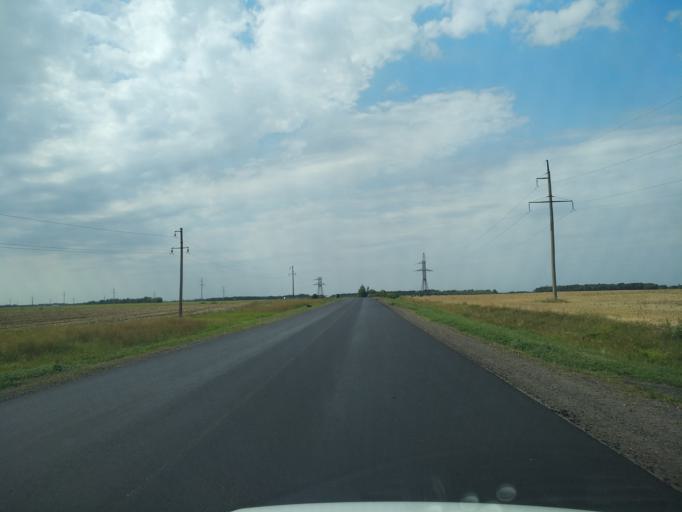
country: RU
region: Voronezj
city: Pereleshino
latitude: 51.7846
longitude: 40.1410
